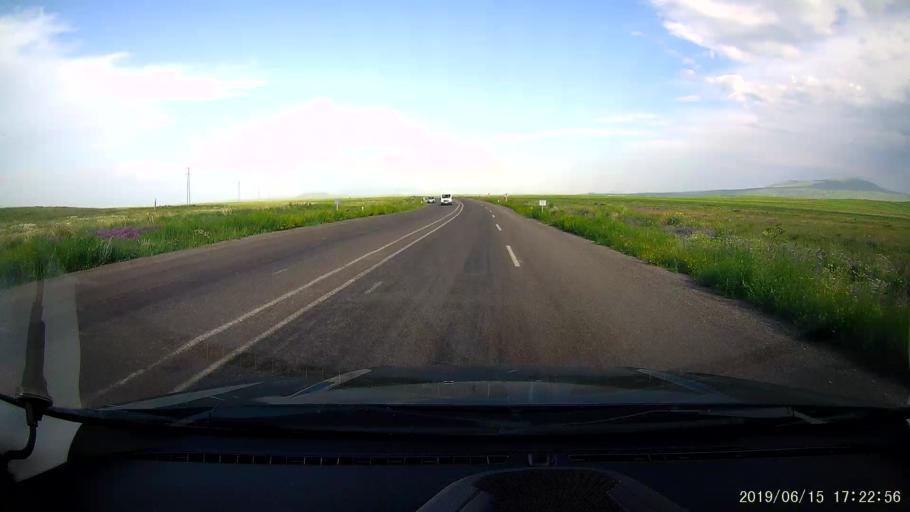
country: TR
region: Kars
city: Basgedikler
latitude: 40.6183
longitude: 43.3525
